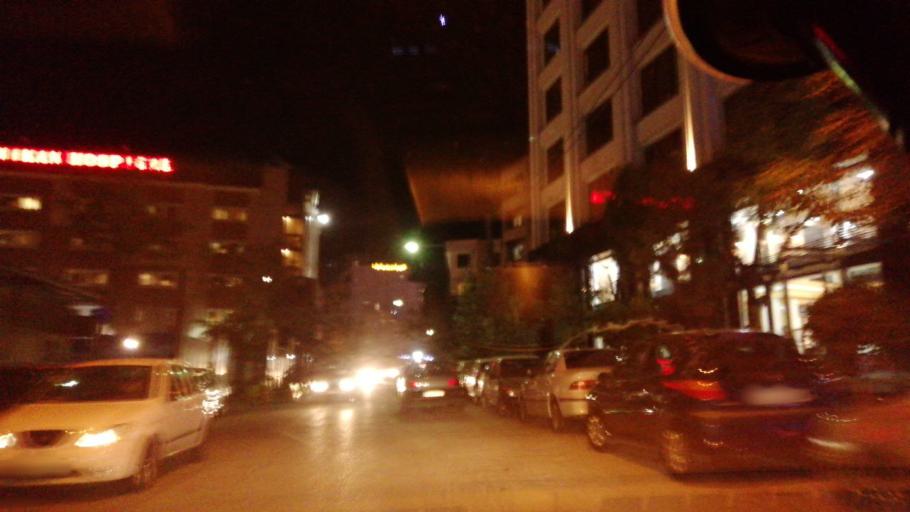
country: IR
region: Tehran
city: Tajrish
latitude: 35.7999
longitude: 51.4905
